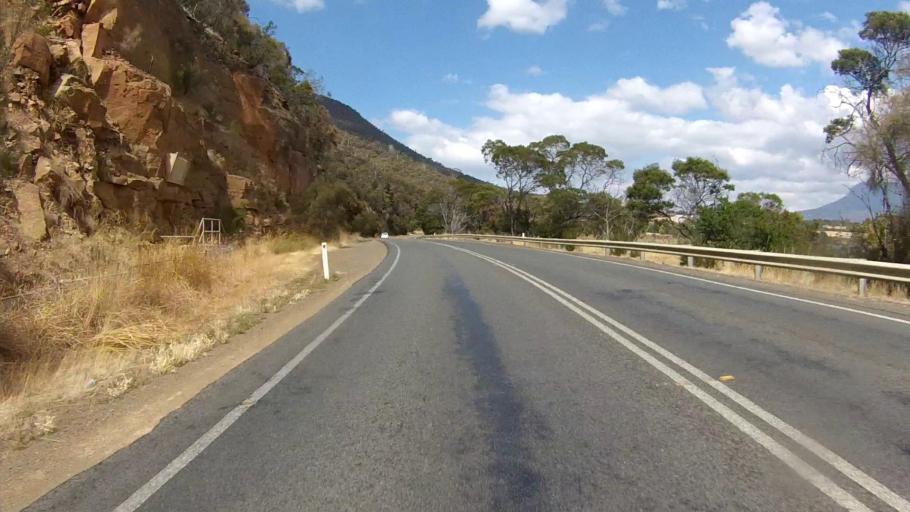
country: AU
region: Tasmania
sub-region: Brighton
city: Old Beach
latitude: -42.7878
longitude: 147.2915
